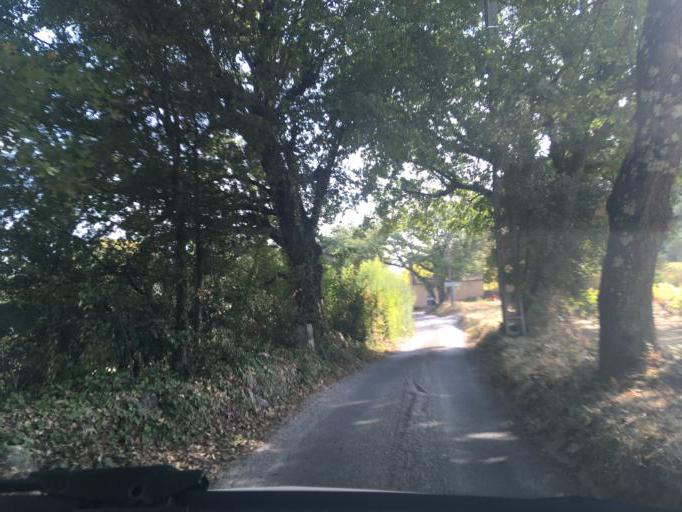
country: FR
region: Provence-Alpes-Cote d'Azur
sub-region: Departement du Var
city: Lorgues
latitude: 43.4855
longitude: 6.3971
